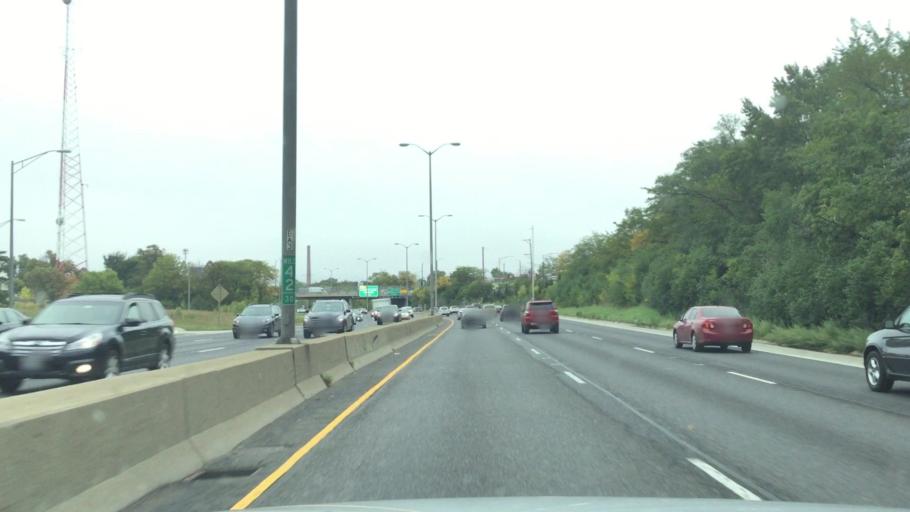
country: US
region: Illinois
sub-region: Cook County
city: Lincolnwood
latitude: 41.9780
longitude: -87.7470
